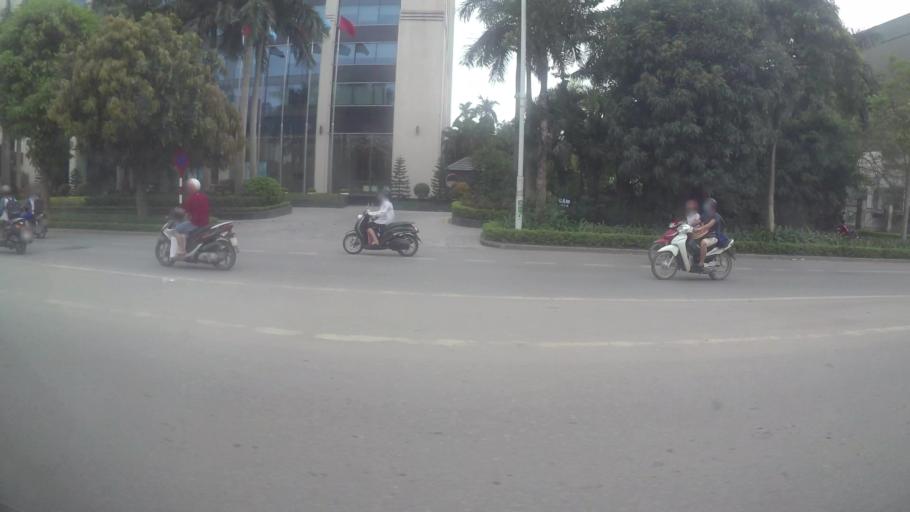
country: VN
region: Ha Noi
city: Cau Dien
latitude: 21.0282
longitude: 105.7672
